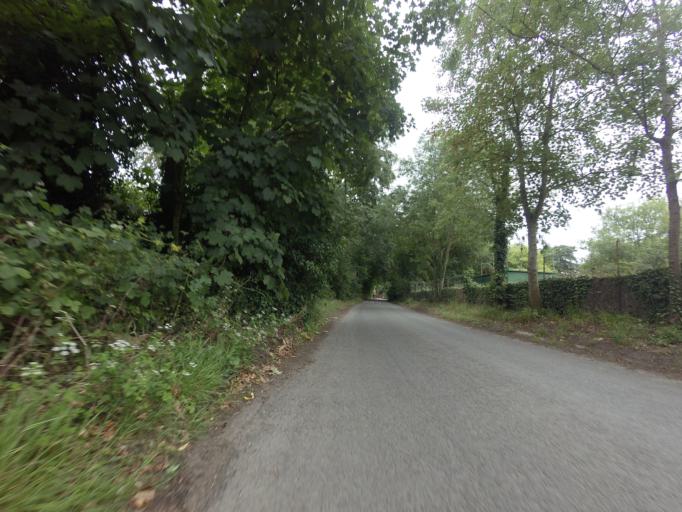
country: GB
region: England
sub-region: Kent
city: West Malling
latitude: 51.3034
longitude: 0.4127
